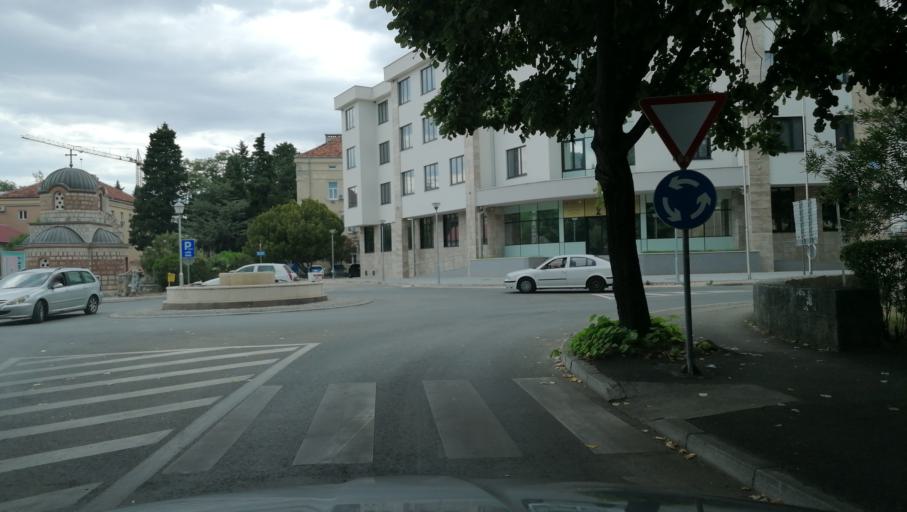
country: BA
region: Republika Srpska
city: Trebinje
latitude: 42.7105
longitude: 18.3428
